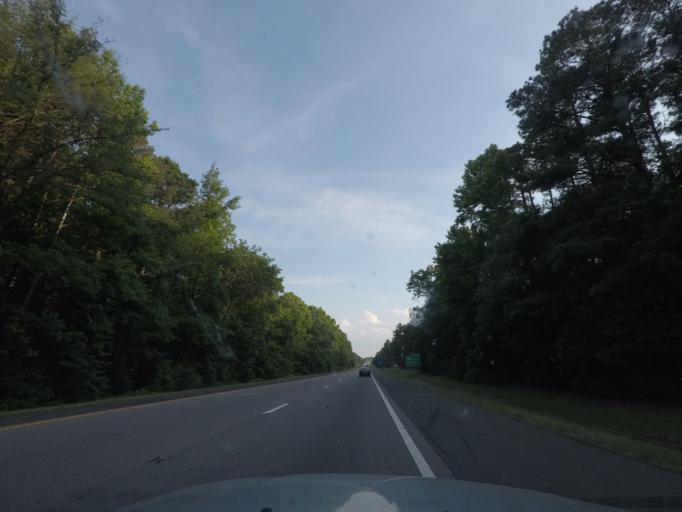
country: US
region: North Carolina
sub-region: Granville County
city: Butner
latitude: 36.0937
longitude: -78.7605
